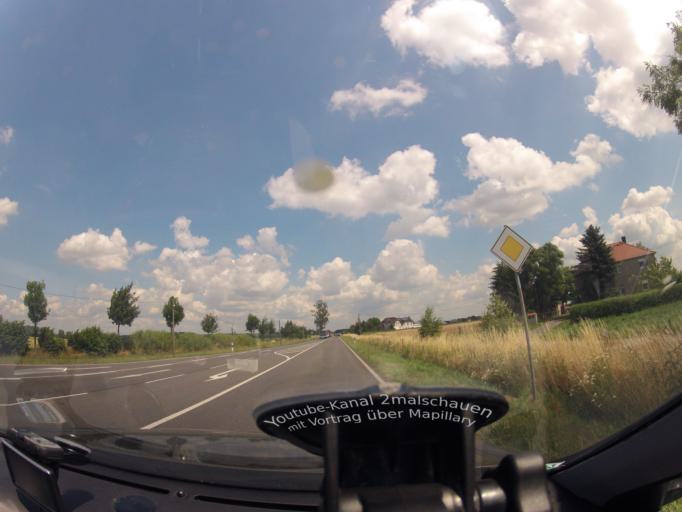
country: DE
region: Saxony
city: Mockrehna
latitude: 51.5108
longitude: 12.8250
